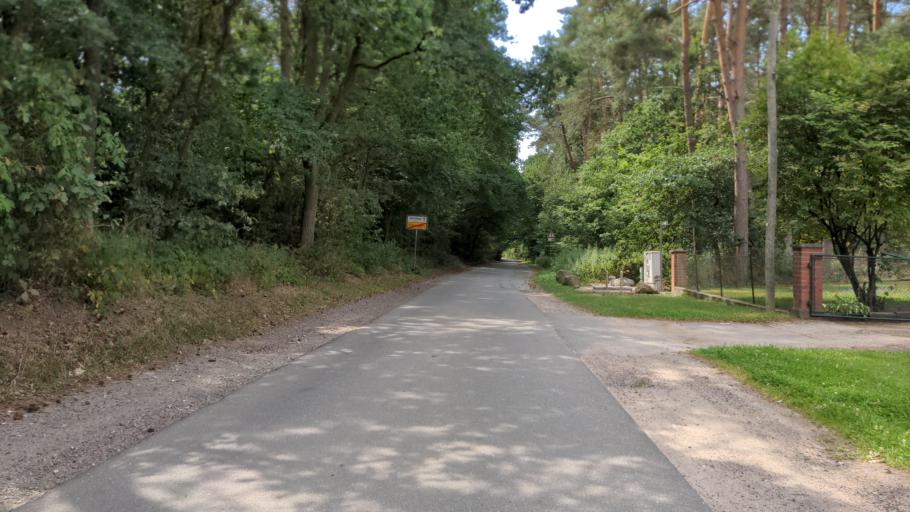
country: DE
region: Schleswig-Holstein
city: Gross Gronau
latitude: 53.8484
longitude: 10.7909
